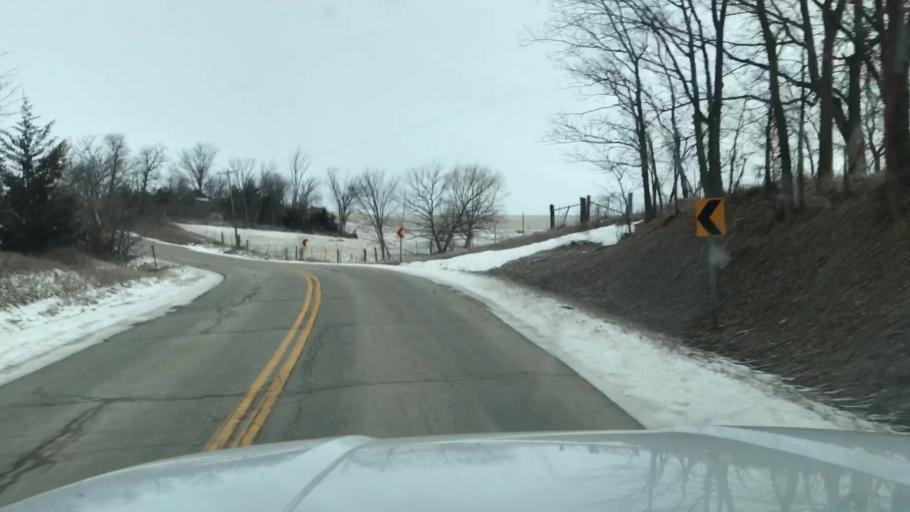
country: US
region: Missouri
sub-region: Andrew County
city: Savannah
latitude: 40.0245
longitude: -94.9193
